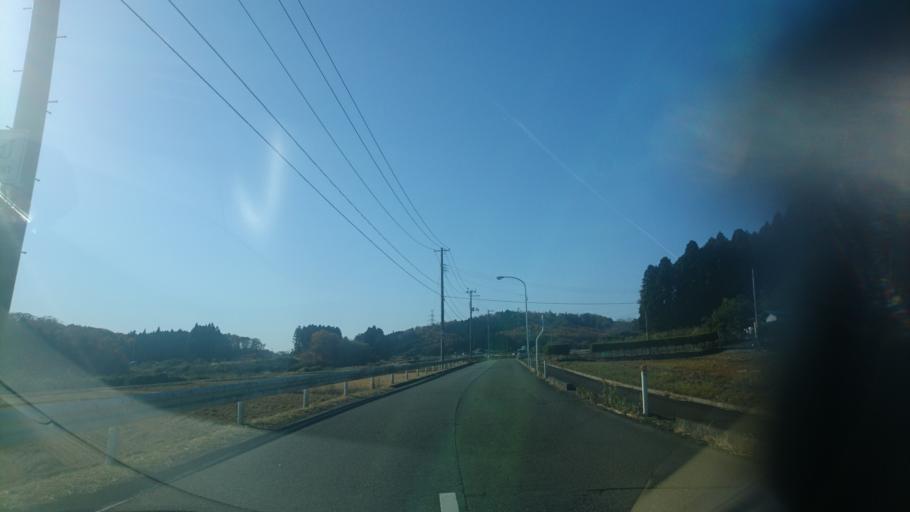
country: JP
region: Miyagi
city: Tomiya
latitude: 38.4079
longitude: 140.8724
